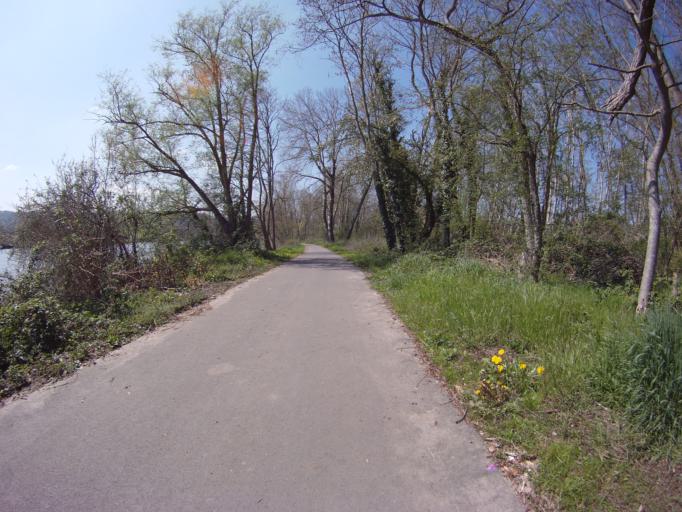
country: FR
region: Lorraine
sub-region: Departement de Meurthe-et-Moselle
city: Belleville
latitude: 48.8250
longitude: 6.0990
